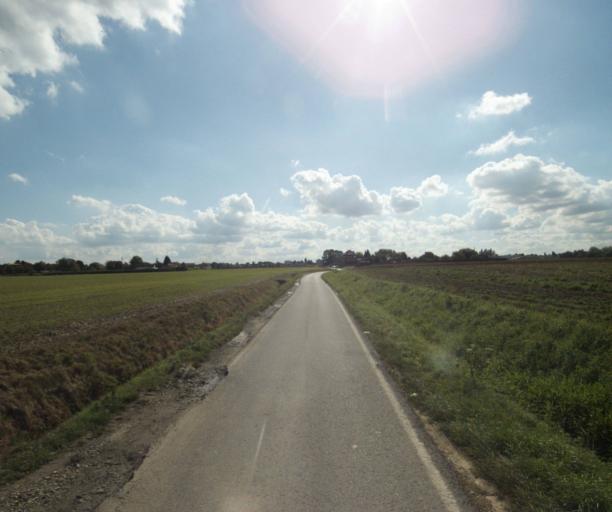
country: FR
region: Nord-Pas-de-Calais
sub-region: Departement du Nord
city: La Bassee
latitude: 50.5486
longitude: 2.8080
